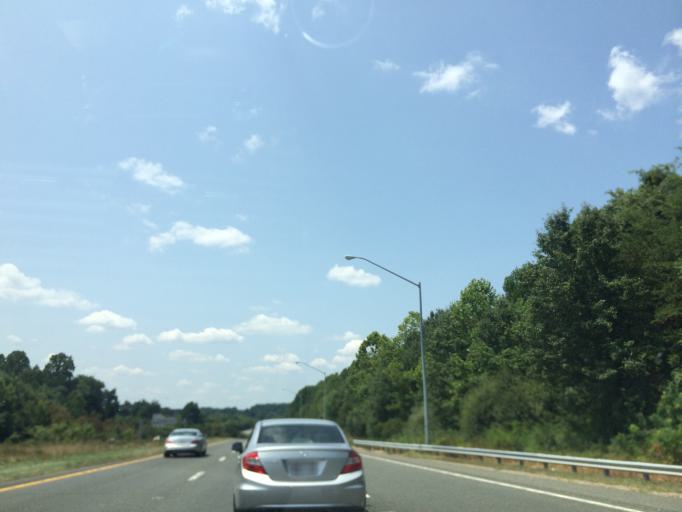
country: US
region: Maryland
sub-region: Howard County
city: Riverside
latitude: 39.1836
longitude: -76.8847
